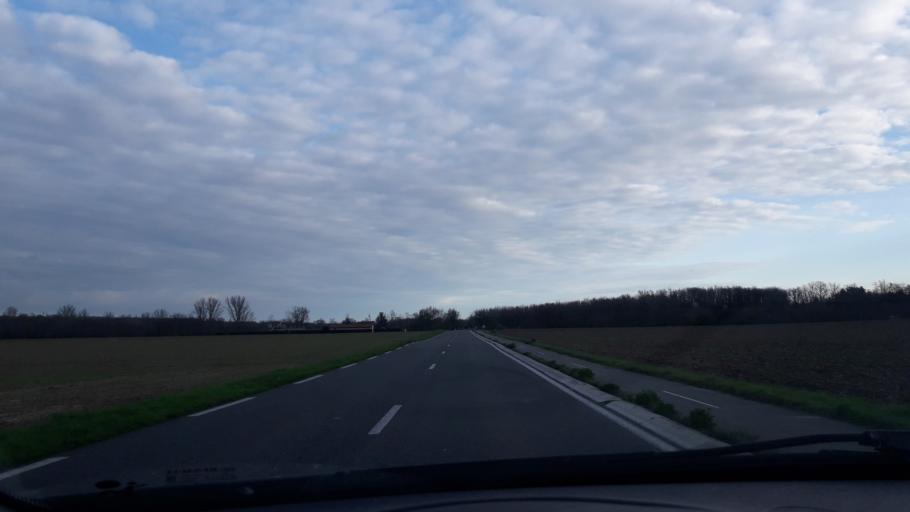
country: FR
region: Midi-Pyrenees
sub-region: Departement de la Haute-Garonne
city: Levignac
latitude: 43.6814
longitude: 1.2115
